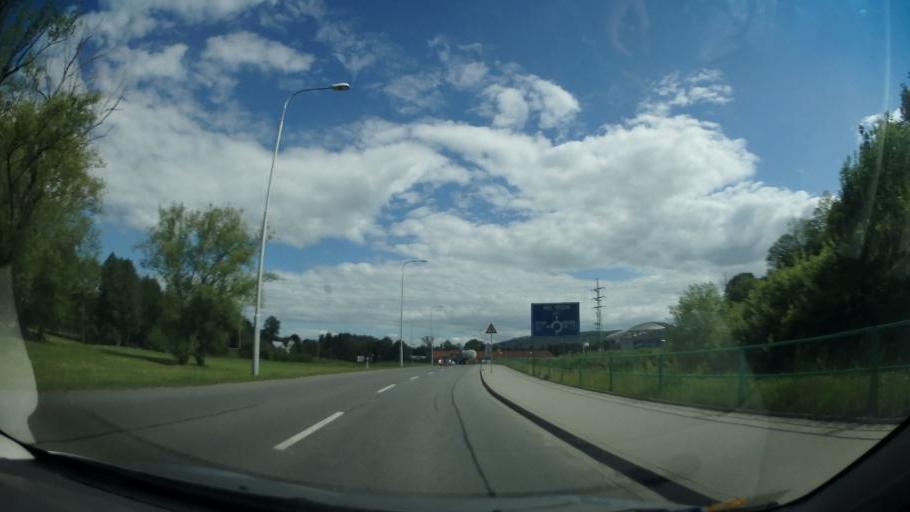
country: CZ
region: Pardubicky
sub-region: Okres Svitavy
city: Moravska Trebova
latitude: 49.7491
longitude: 16.6570
